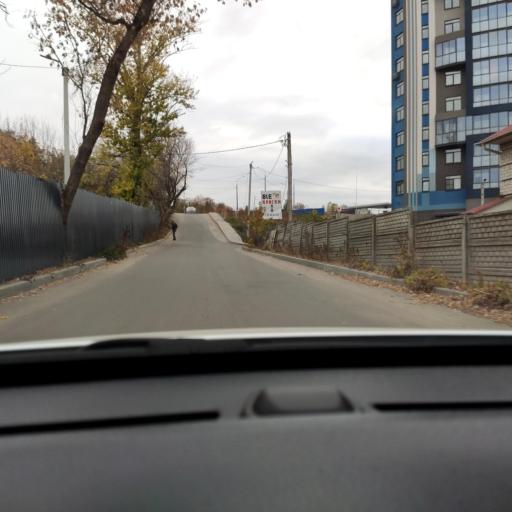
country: RU
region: Voronezj
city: Voronezh
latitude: 51.6953
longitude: 39.2332
